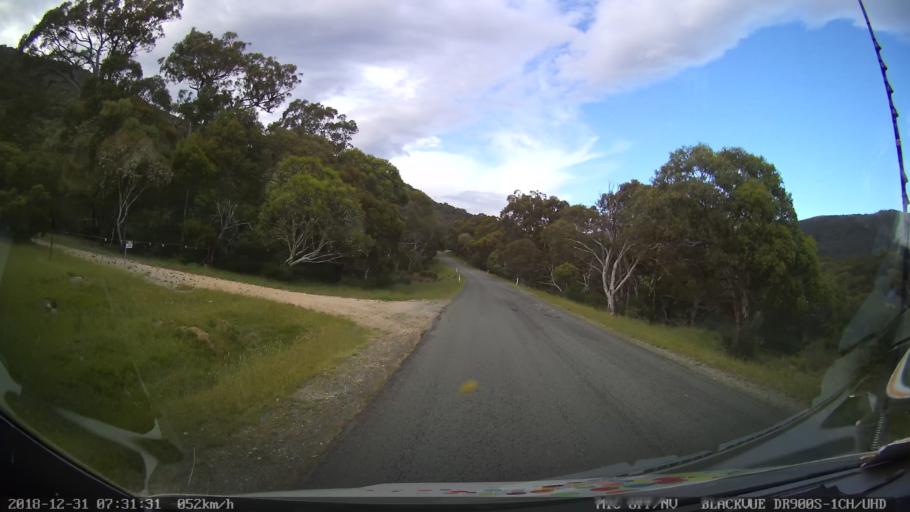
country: AU
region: New South Wales
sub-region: Snowy River
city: Jindabyne
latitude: -36.3262
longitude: 148.4725
